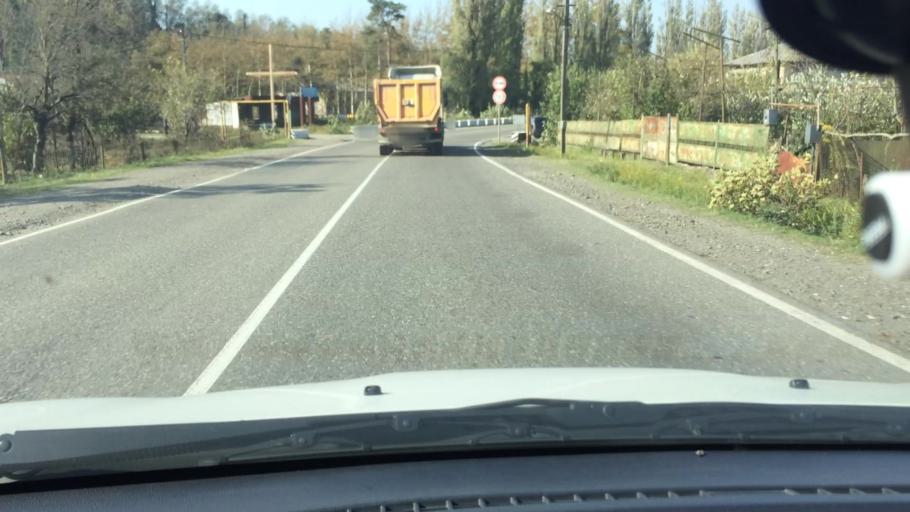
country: GE
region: Guria
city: Lanchkhuti
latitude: 42.0887
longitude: 42.0166
